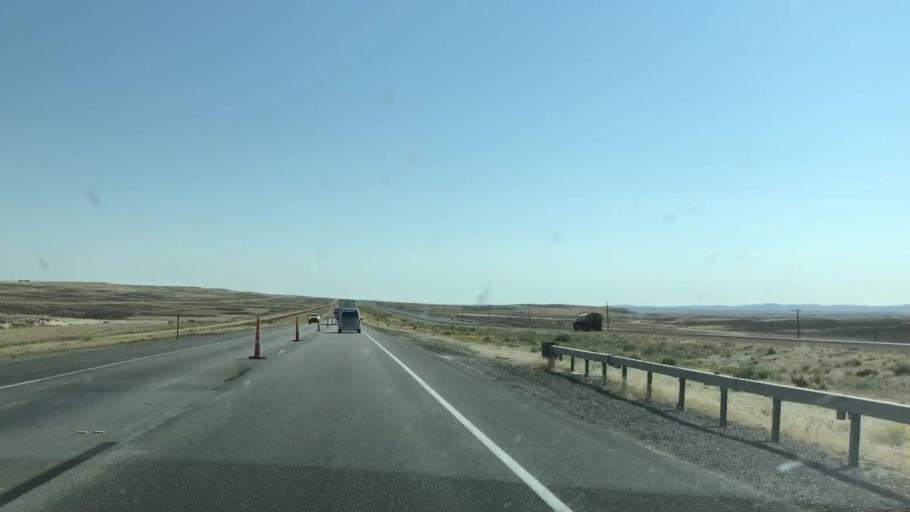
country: US
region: Wyoming
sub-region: Carbon County
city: Rawlins
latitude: 41.7456
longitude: -107.6179
